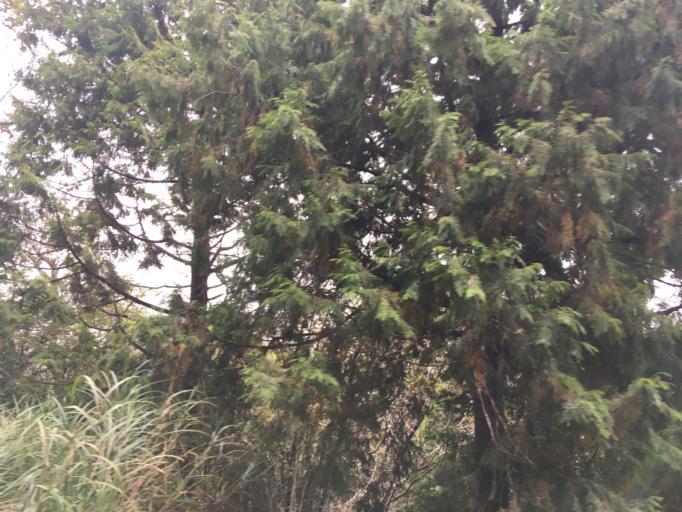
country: TW
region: Taiwan
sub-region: Yilan
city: Yilan
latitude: 24.4882
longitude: 121.5344
